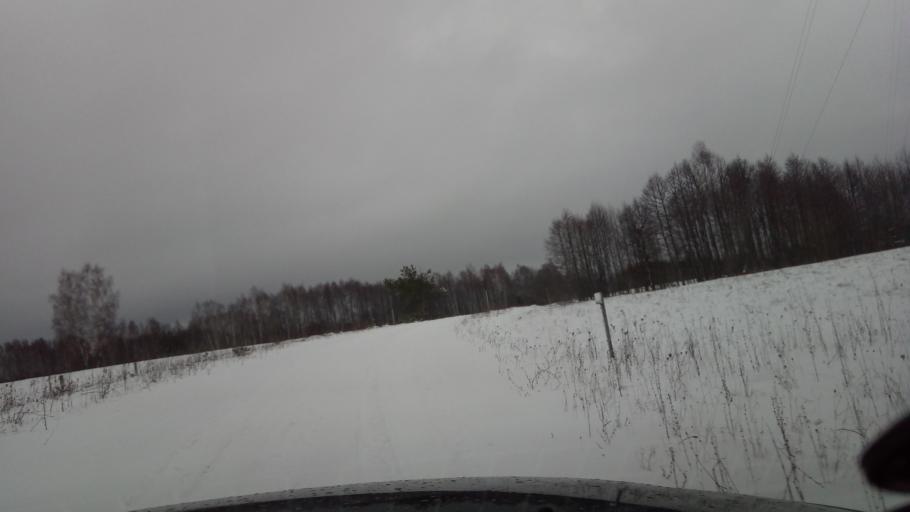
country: LT
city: Zarasai
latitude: 55.6207
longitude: 25.9454
